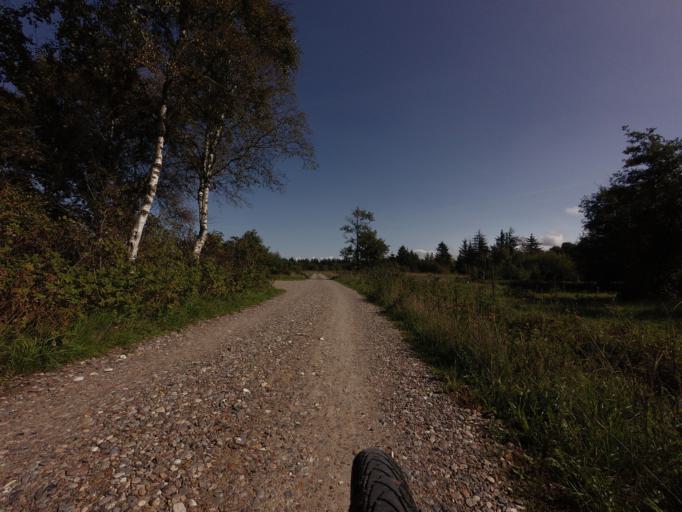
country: DK
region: North Denmark
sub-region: Hjorring Kommune
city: Hirtshals
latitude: 57.5842
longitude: 10.0457
